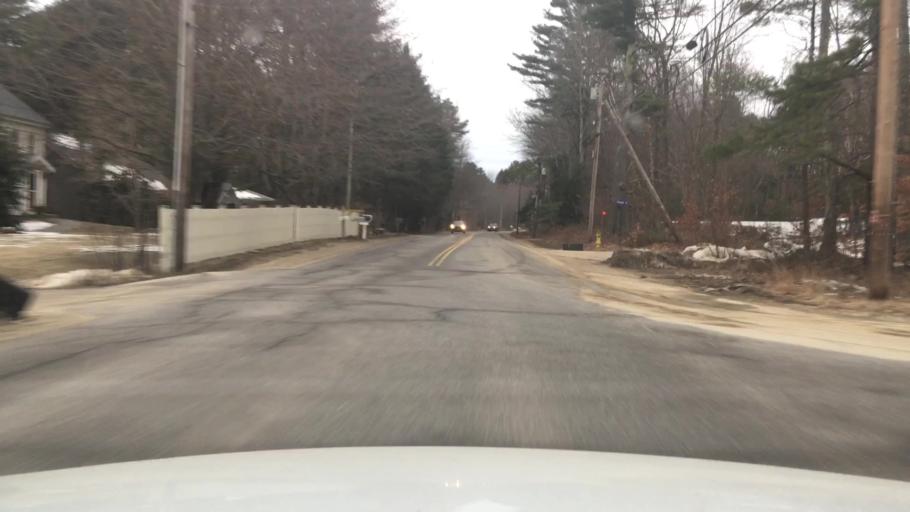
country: US
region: Maine
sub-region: Sagadahoc County
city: Topsham
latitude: 43.8998
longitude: -70.0001
